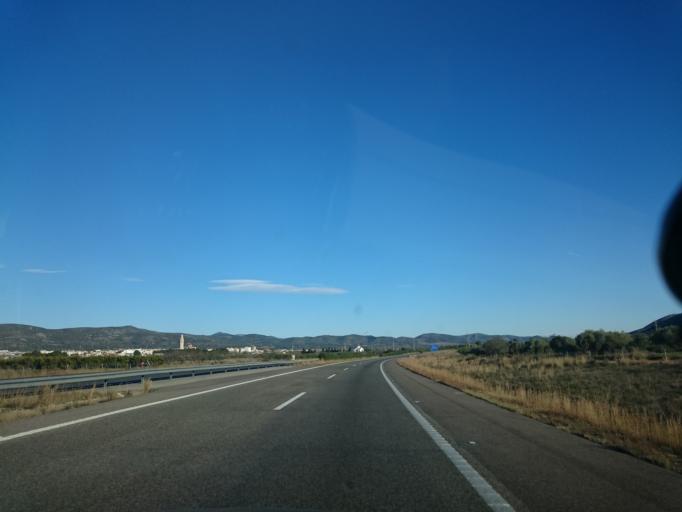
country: ES
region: Valencia
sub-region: Provincia de Castello
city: Alcala de Xivert
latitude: 40.2890
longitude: 0.2288
